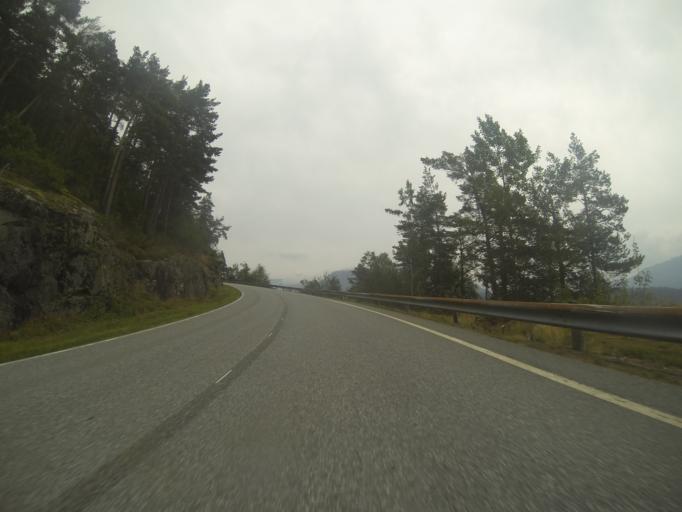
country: NO
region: Rogaland
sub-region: Suldal
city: Sand
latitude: 59.5376
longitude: 6.2628
